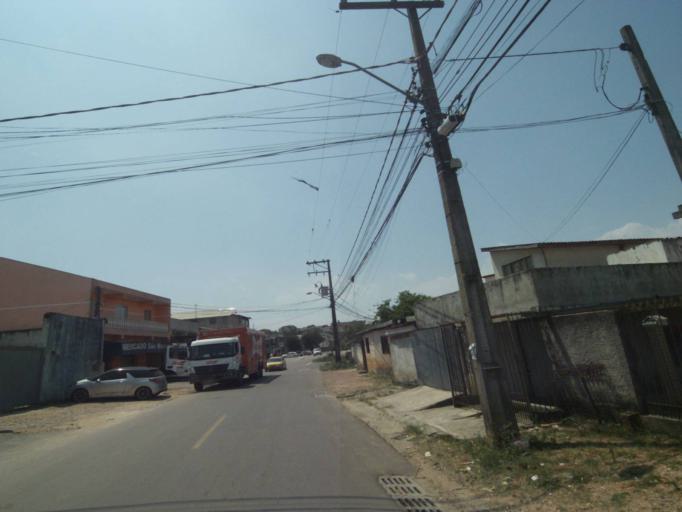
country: BR
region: Parana
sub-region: Curitiba
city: Curitiba
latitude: -25.4838
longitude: -49.3145
